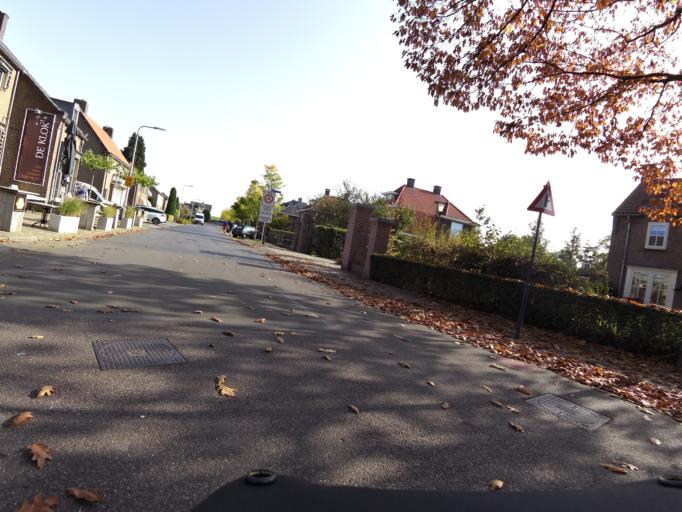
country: NL
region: Gelderland
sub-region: Gemeente Groesbeek
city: Berg en Dal
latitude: 51.8751
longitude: 5.9707
